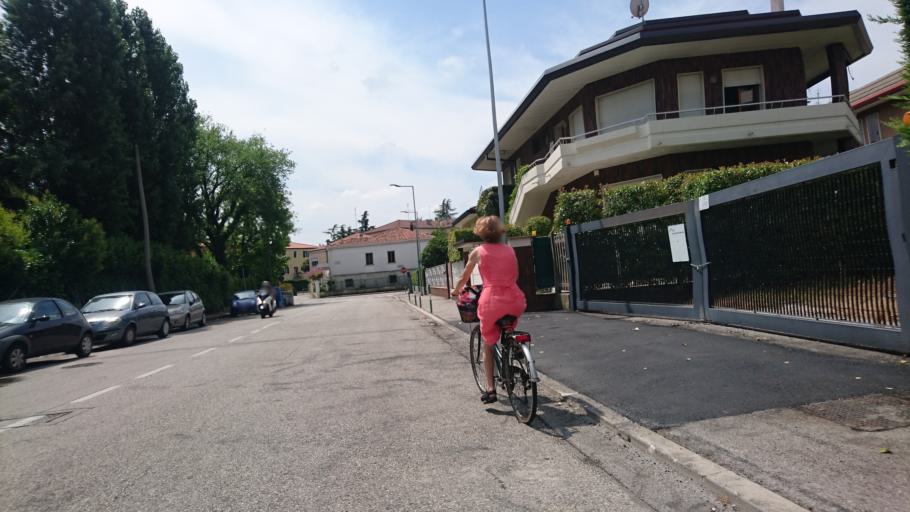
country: IT
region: Veneto
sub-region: Provincia di Padova
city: Padova
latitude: 45.4023
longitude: 11.8576
